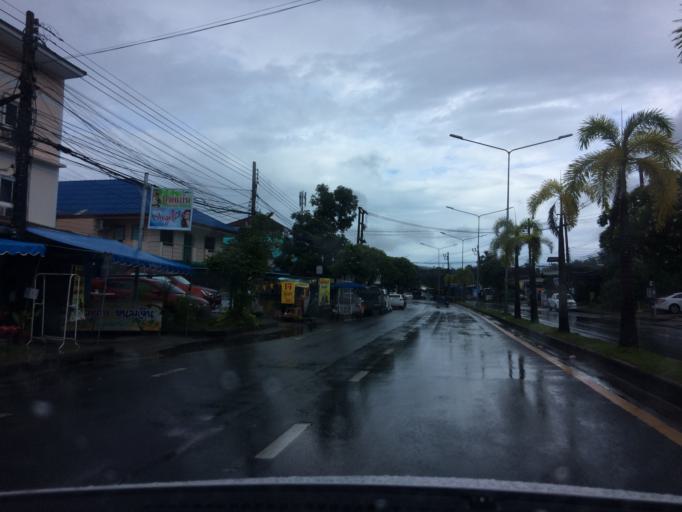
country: TH
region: Phuket
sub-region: Amphoe Kathu
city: Kathu
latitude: 7.9170
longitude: 98.3314
